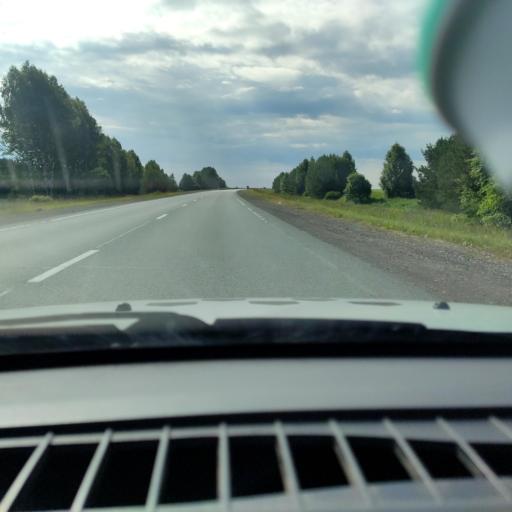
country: RU
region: Perm
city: Suksun
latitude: 56.9088
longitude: 57.5908
